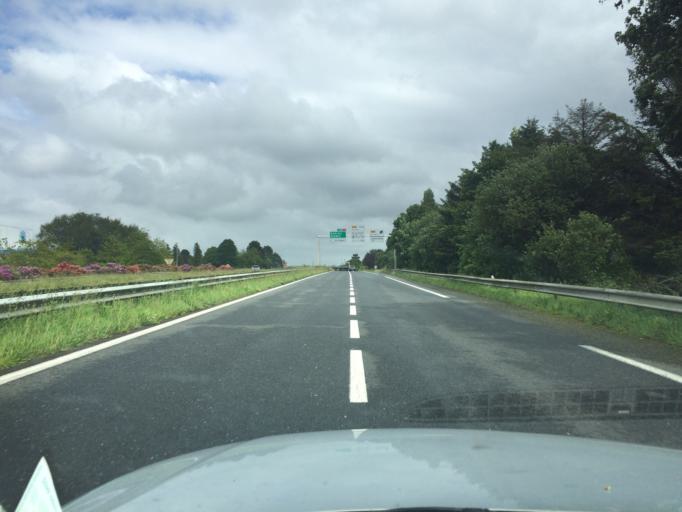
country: FR
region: Brittany
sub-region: Departement du Finistere
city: Landivisiau
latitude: 48.5183
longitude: -4.0612
